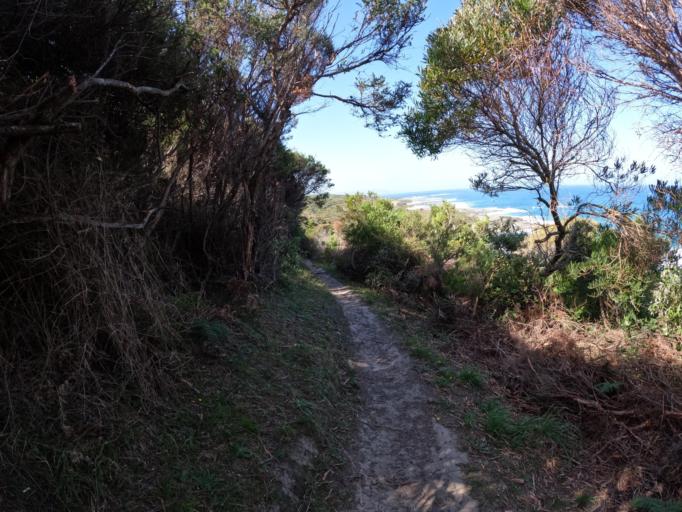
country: AU
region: Victoria
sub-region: Colac-Otway
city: Apollo Bay
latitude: -38.7897
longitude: 143.6476
